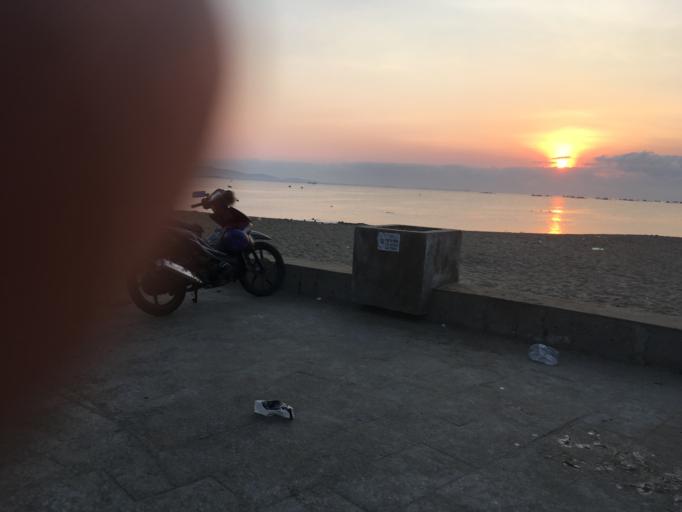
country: VN
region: Ninh Thuan
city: Khanh Hai
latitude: 11.5625
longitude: 109.0245
